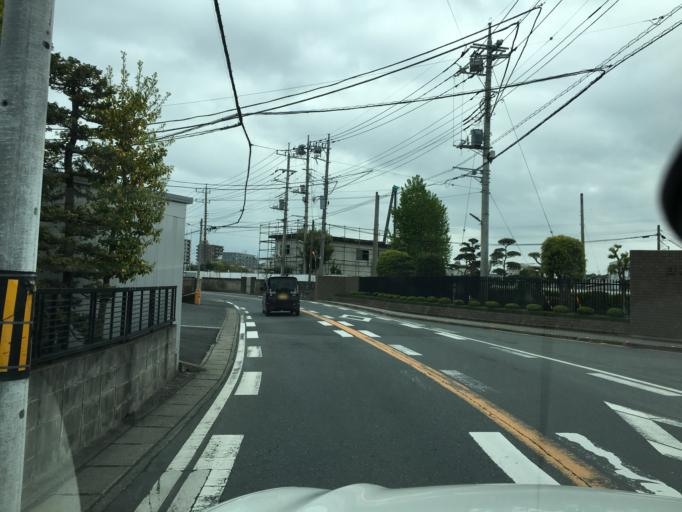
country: JP
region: Saitama
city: Koshigaya
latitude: 35.8634
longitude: 139.7857
